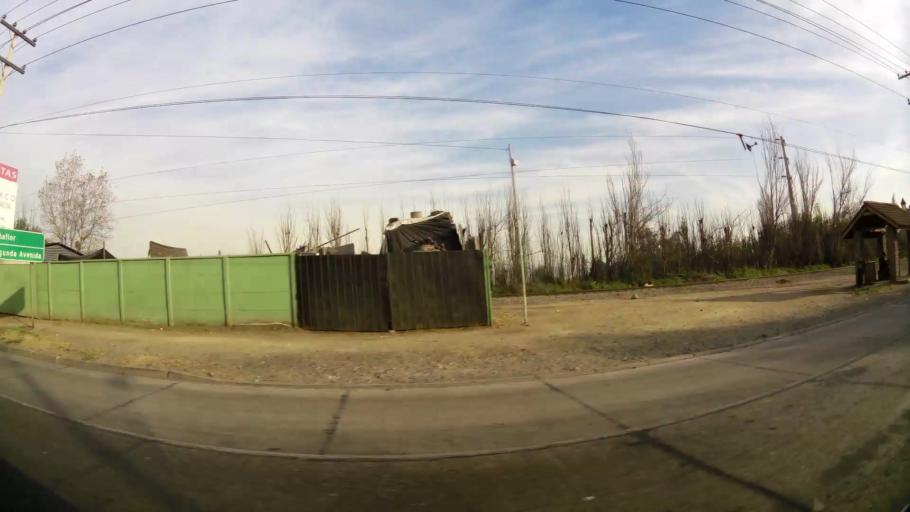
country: CL
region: Santiago Metropolitan
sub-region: Provincia de Talagante
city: Penaflor
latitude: -33.5562
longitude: -70.7990
